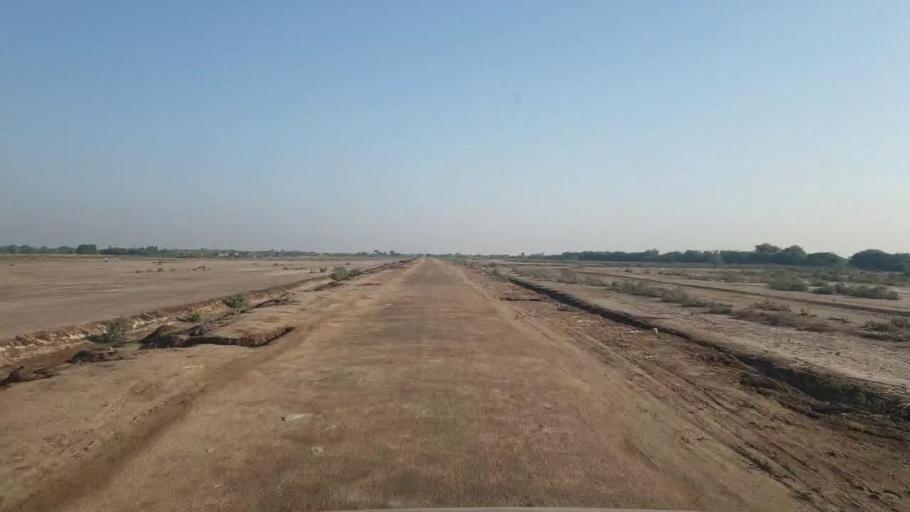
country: PK
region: Sindh
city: Badin
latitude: 24.7189
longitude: 68.8609
